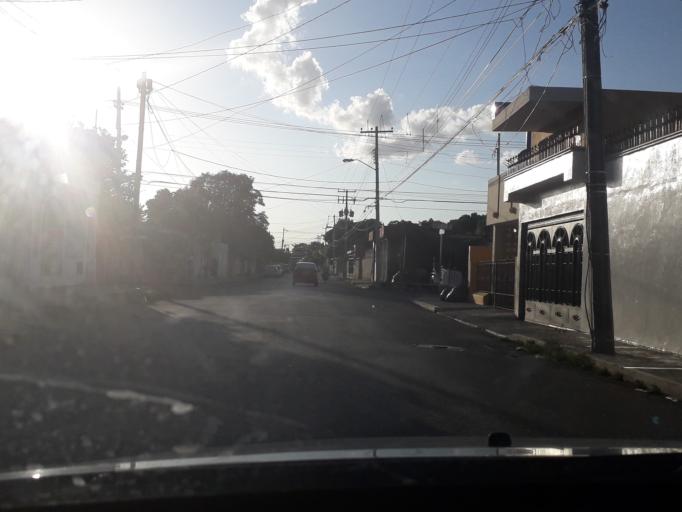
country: MX
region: Yucatan
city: Merida
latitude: 20.9664
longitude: -89.6457
